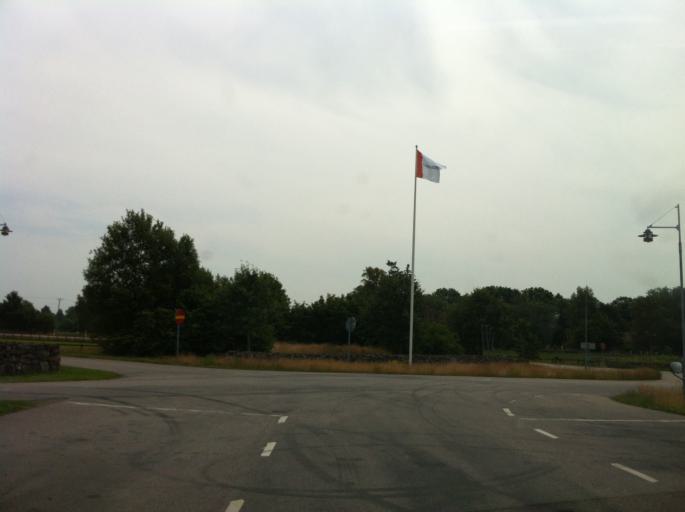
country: SE
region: Kalmar
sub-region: Torsas Kommun
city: Torsas
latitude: 56.3220
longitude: 16.0335
